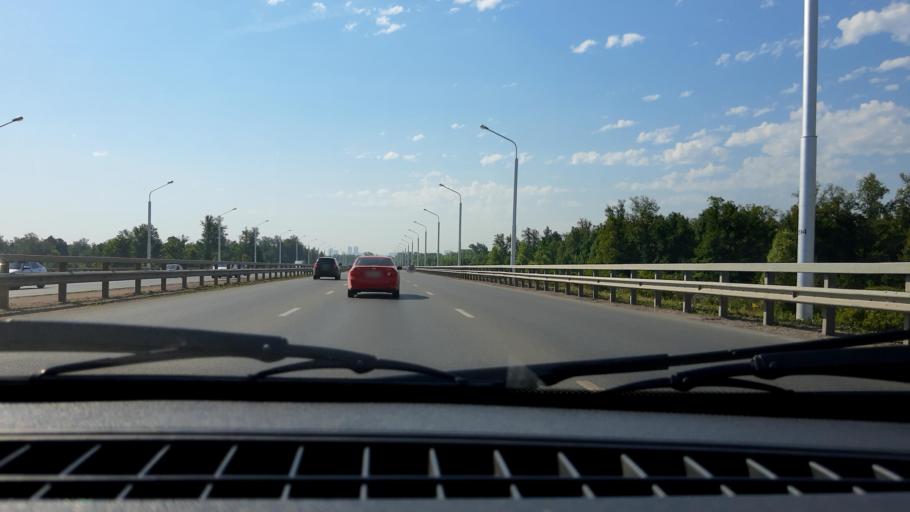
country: RU
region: Bashkortostan
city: Mikhaylovka
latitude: 54.7885
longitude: 55.9087
